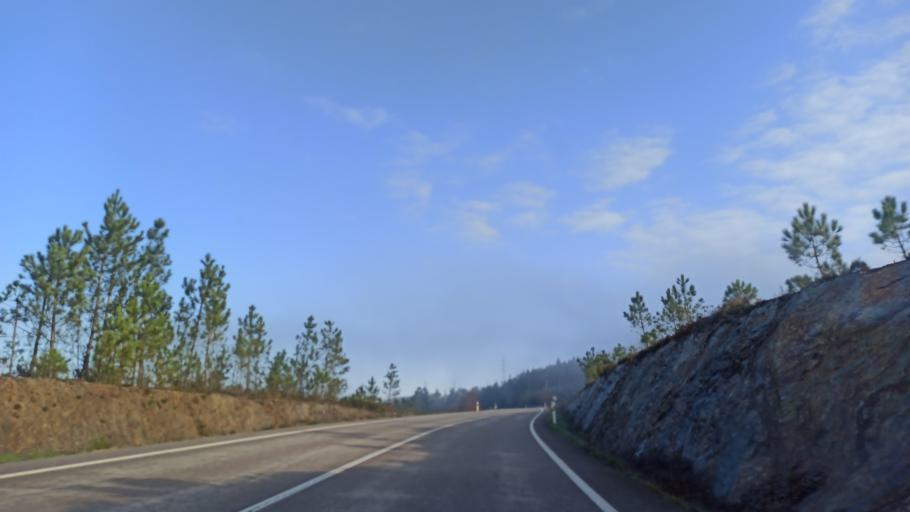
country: ES
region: Galicia
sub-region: Provincia da Coruna
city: As Pontes de Garcia Rodriguez
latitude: 43.4742
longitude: -7.8533
